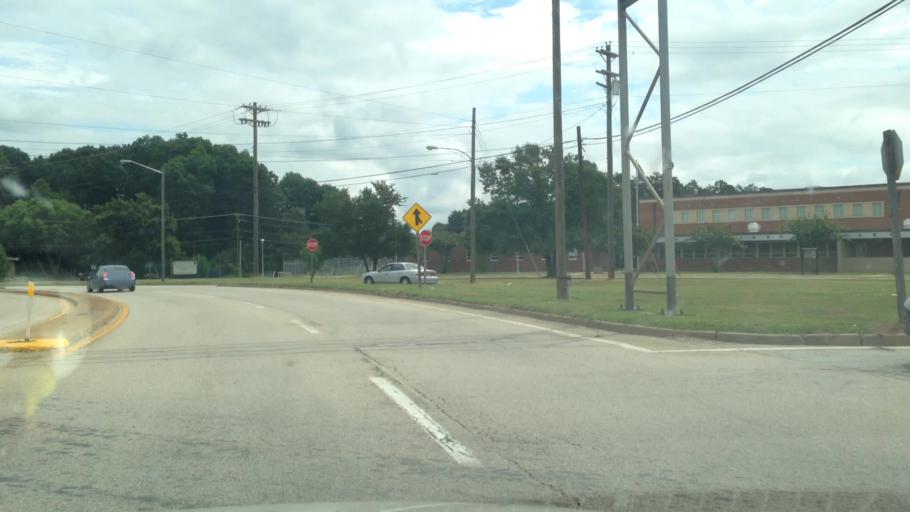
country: US
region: Virginia
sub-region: City of Danville
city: Danville
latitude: 36.6364
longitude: -79.3873
